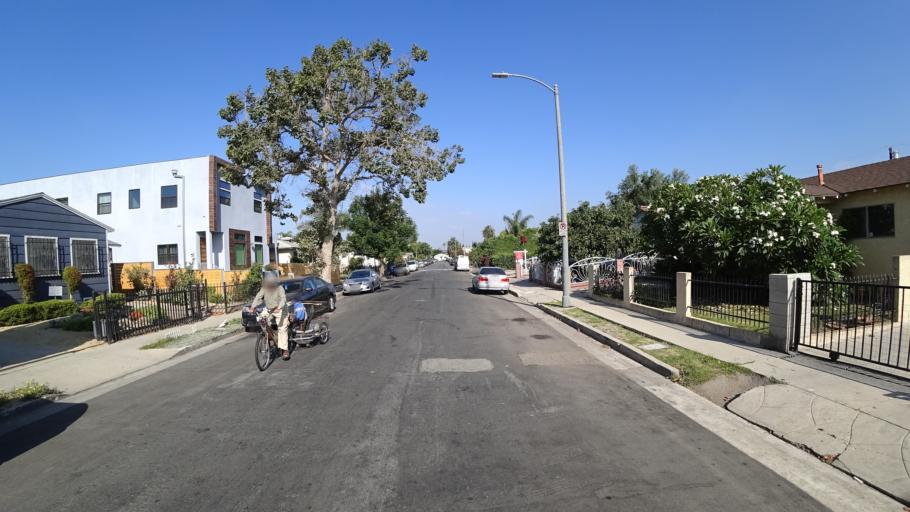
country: US
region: California
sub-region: Los Angeles County
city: Culver City
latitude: 34.0291
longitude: -118.3657
